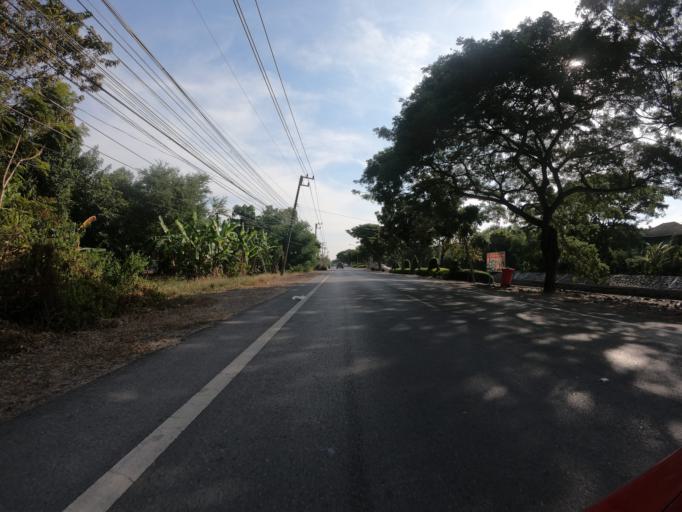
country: TH
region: Pathum Thani
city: Lam Luk Ka
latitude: 13.9719
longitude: 100.7285
